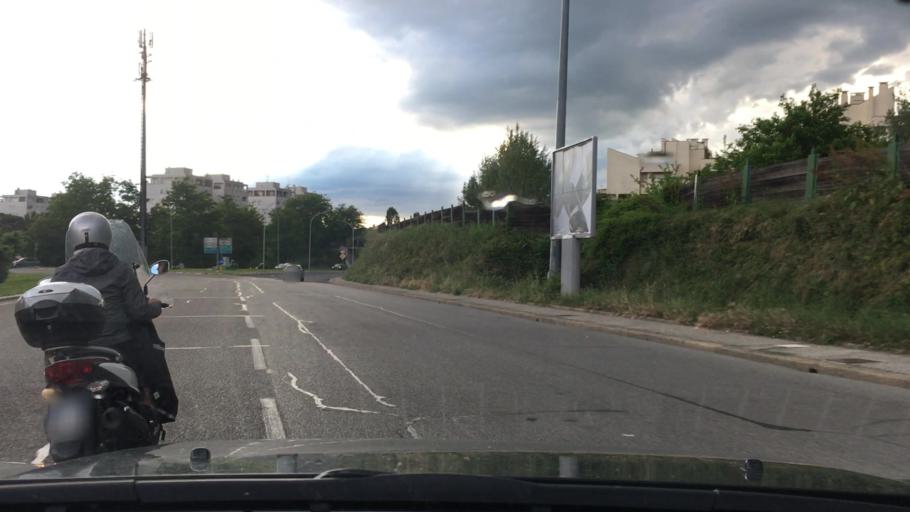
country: IT
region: Emilia-Romagna
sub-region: Provincia di Bologna
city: Bologna
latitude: 44.5014
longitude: 11.3050
